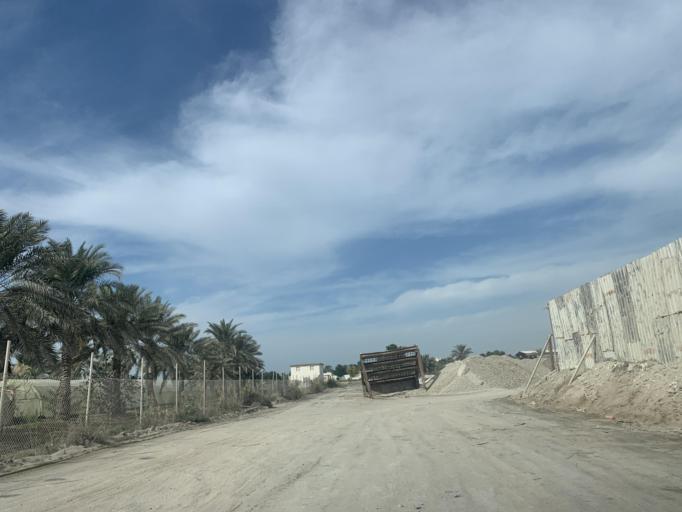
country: BH
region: Central Governorate
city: Madinat Hamad
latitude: 26.1172
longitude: 50.4706
